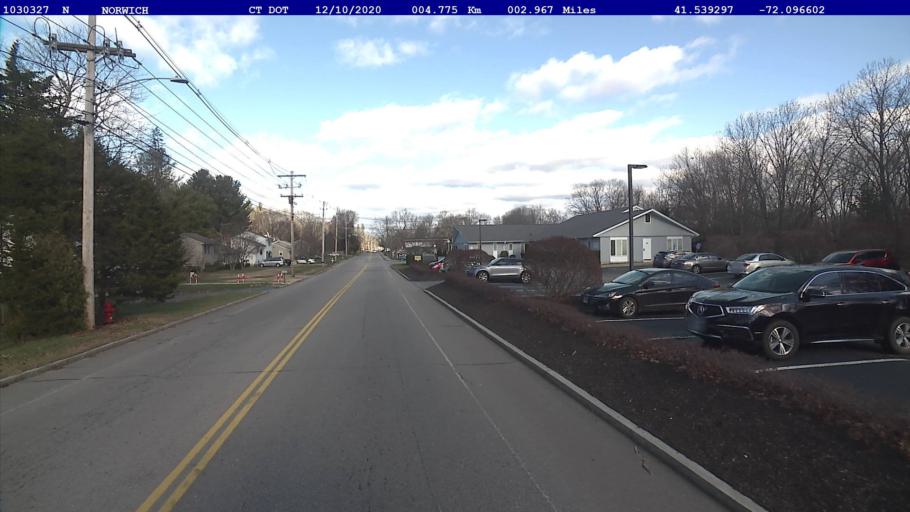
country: US
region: Connecticut
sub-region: New London County
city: Norwich
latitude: 41.5393
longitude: -72.0966
